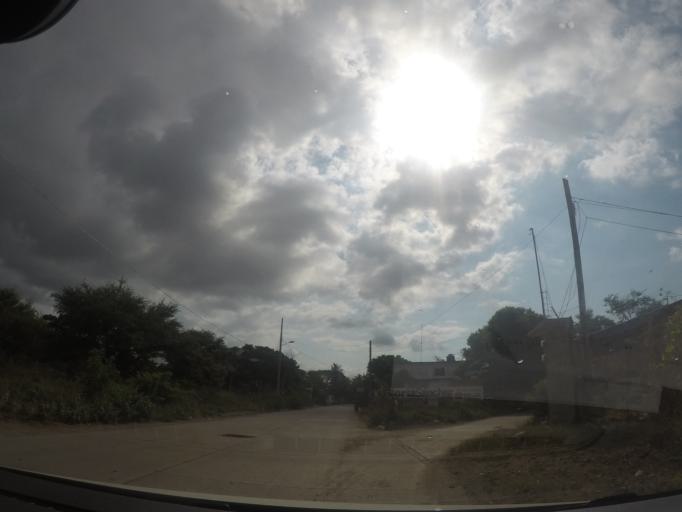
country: MX
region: Oaxaca
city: Juchitan de Zaragoza
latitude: 16.4299
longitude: -95.0315
